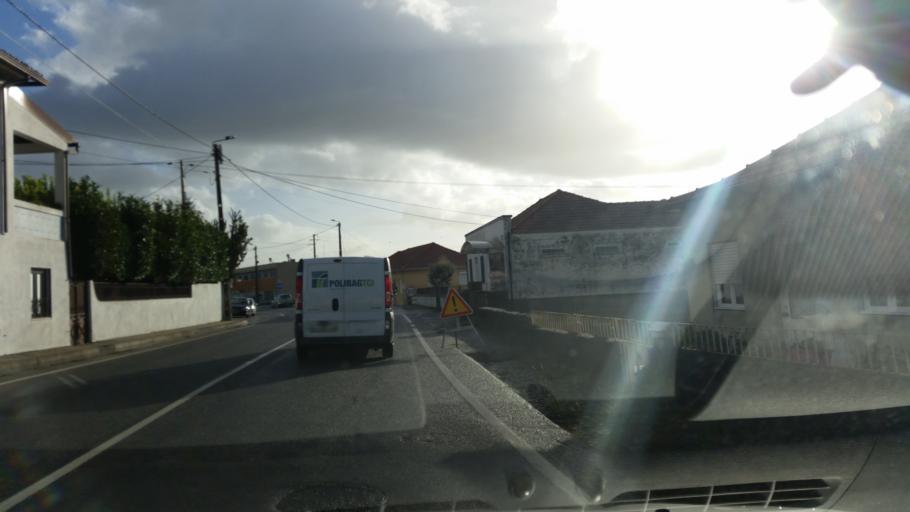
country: PT
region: Braga
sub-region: Guimaraes
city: Lordelo
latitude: 41.3689
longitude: -8.3840
